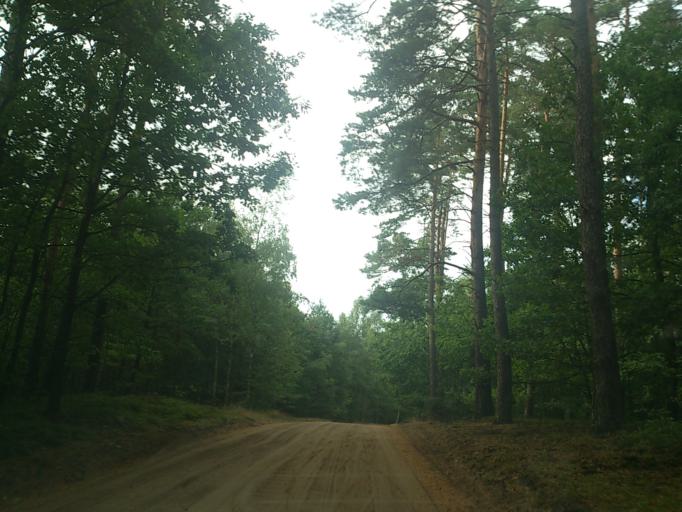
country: PL
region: Greater Poland Voivodeship
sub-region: Powiat poznanski
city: Kobylnica
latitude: 52.5273
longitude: 17.1193
